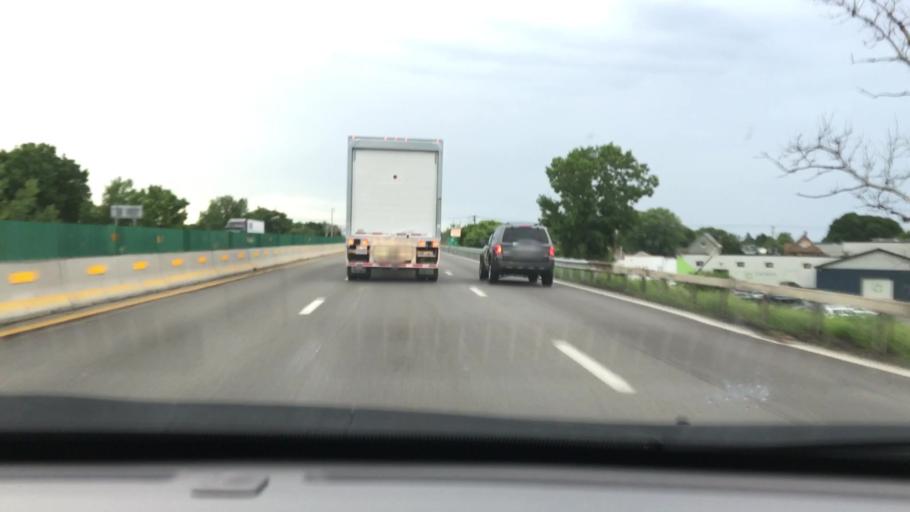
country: US
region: New York
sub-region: Erie County
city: West Seneca
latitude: 42.8419
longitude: -78.7926
